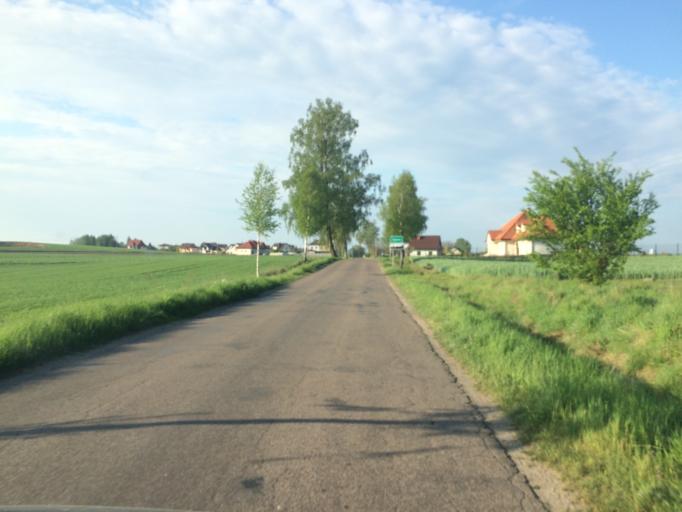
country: PL
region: Warmian-Masurian Voivodeship
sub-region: Powiat dzialdowski
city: Rybno
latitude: 53.3949
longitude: 19.9329
